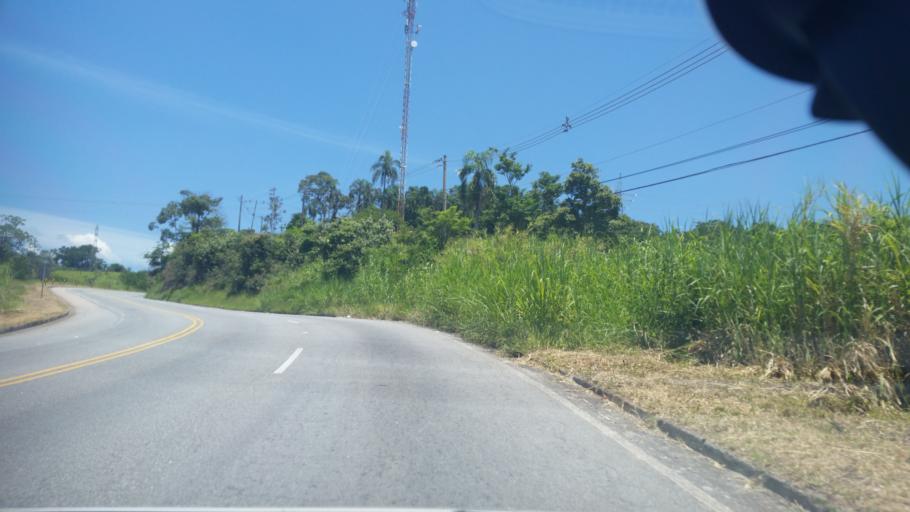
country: BR
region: Sao Paulo
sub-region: Taubate
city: Taubate
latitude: -23.0867
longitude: -45.5433
